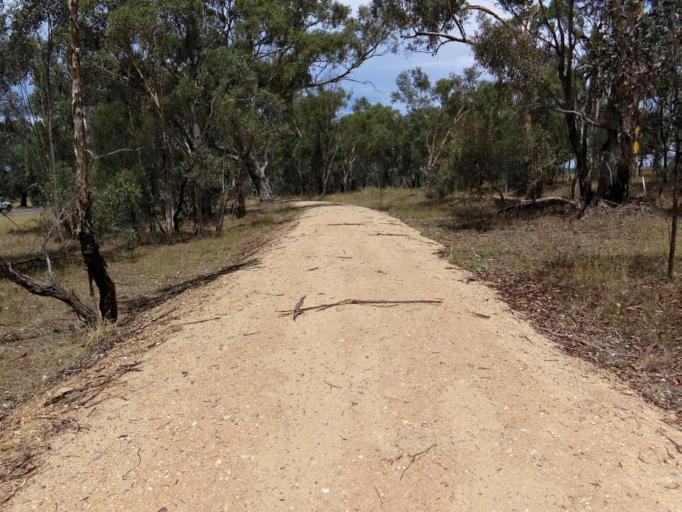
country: AU
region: Victoria
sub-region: Greater Bendigo
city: Kennington
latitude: -36.8780
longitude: 144.6402
